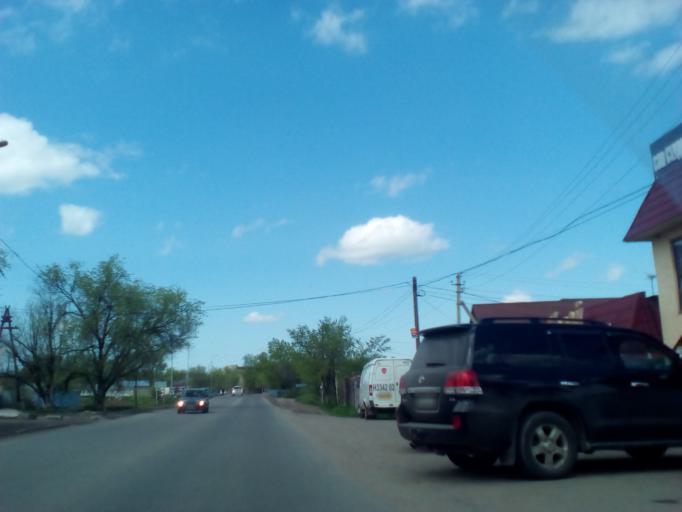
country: KZ
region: Almaty Oblysy
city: Burunday
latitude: 43.2078
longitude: 76.6372
